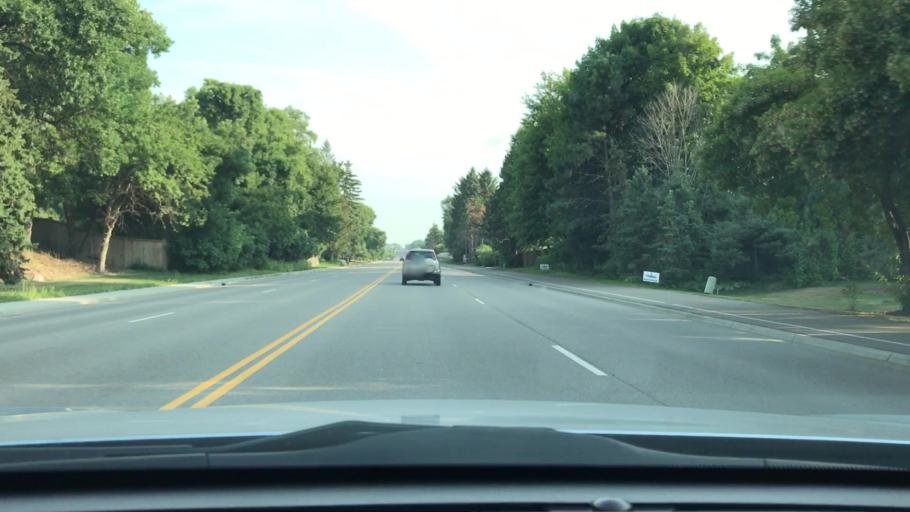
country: US
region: Minnesota
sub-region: Hennepin County
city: Plymouth
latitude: 45.0380
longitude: -93.4818
